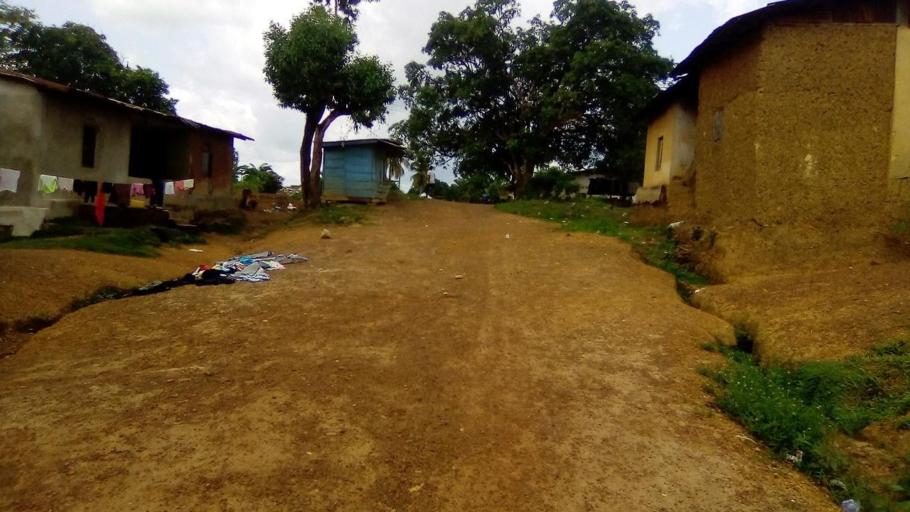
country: SL
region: Southern Province
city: Bo
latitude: 7.9591
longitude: -11.7249
